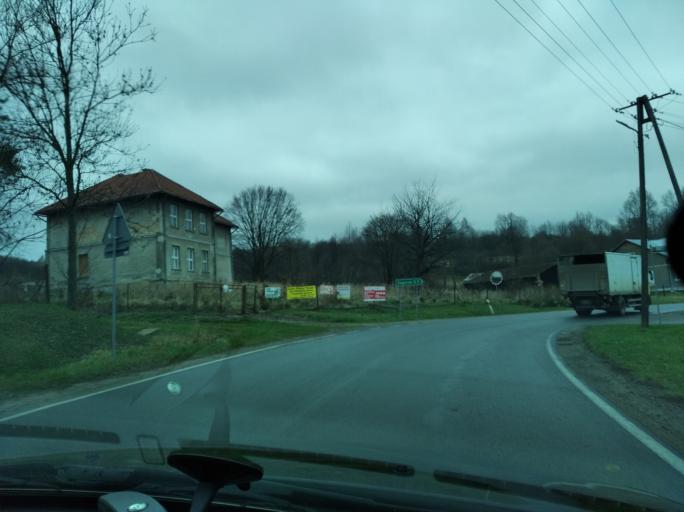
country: PL
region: Subcarpathian Voivodeship
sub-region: Powiat przeworski
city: Manasterz
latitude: 49.9372
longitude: 22.3519
